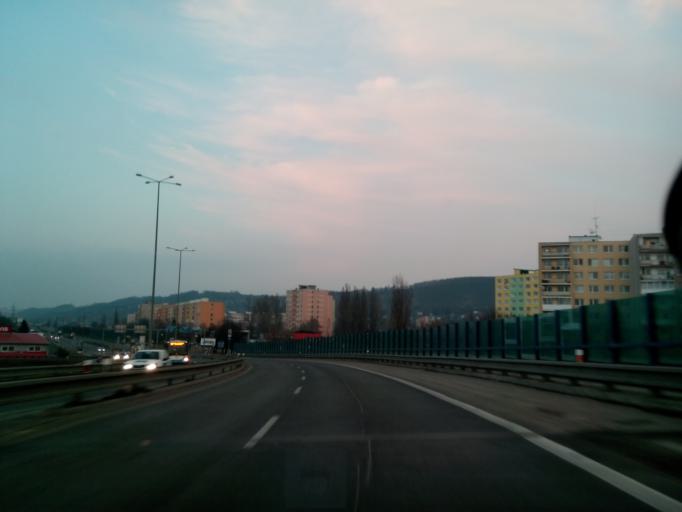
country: SK
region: Kosicky
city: Kosice
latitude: 48.6910
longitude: 21.2797
